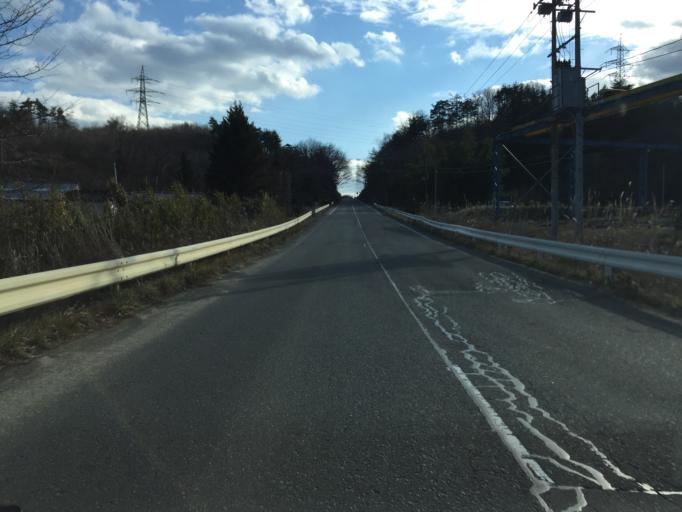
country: JP
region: Fukushima
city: Fukushima-shi
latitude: 37.6809
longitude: 140.4256
